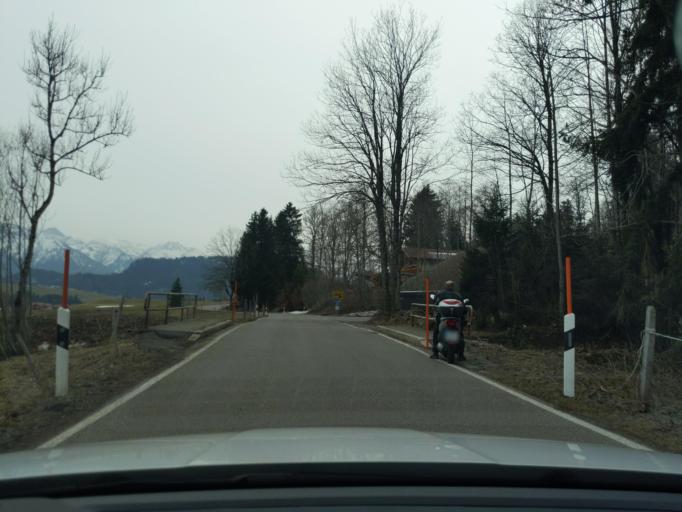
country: DE
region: Bavaria
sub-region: Swabia
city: Bolsterlang
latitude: 47.4664
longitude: 10.2303
